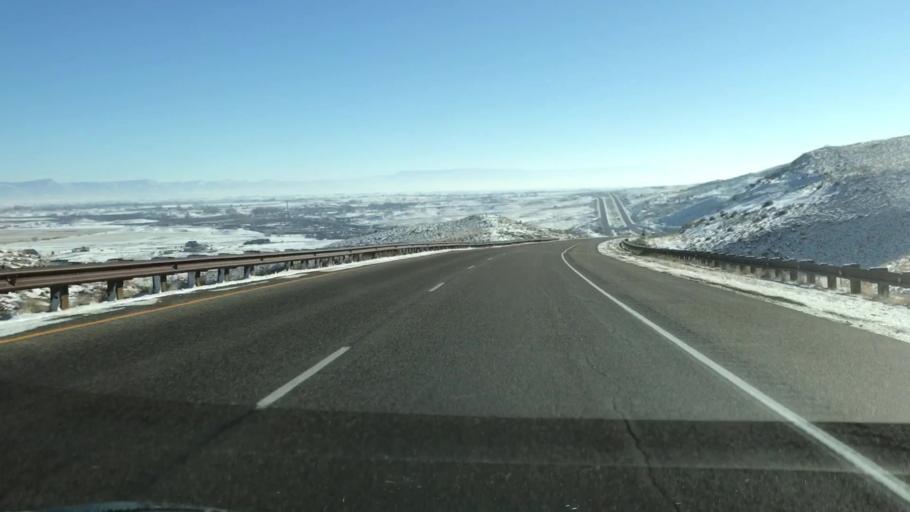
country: US
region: Colorado
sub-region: Mesa County
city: Loma
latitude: 39.2291
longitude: -108.9047
